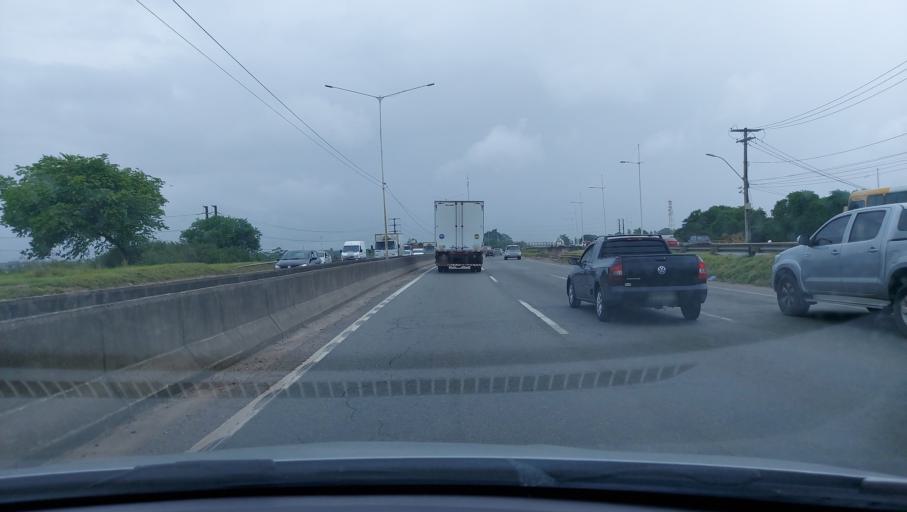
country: BR
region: Bahia
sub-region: Salvador
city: Salvador
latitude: -12.8907
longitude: -38.4446
